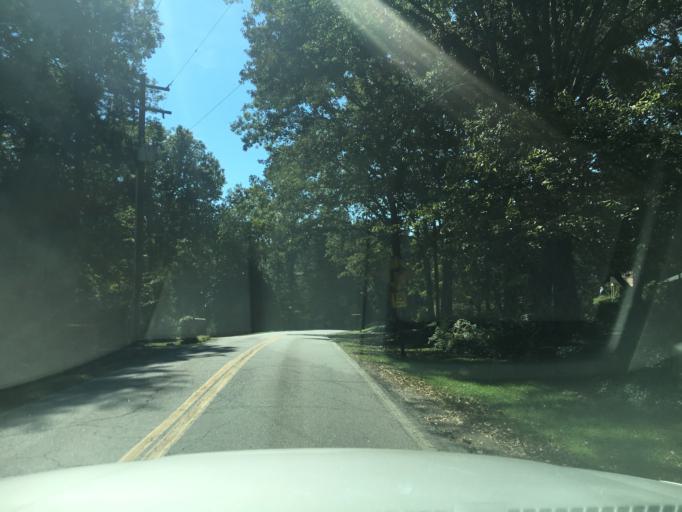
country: US
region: South Carolina
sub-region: Greenville County
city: Taylors
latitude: 34.8991
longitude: -82.2728
